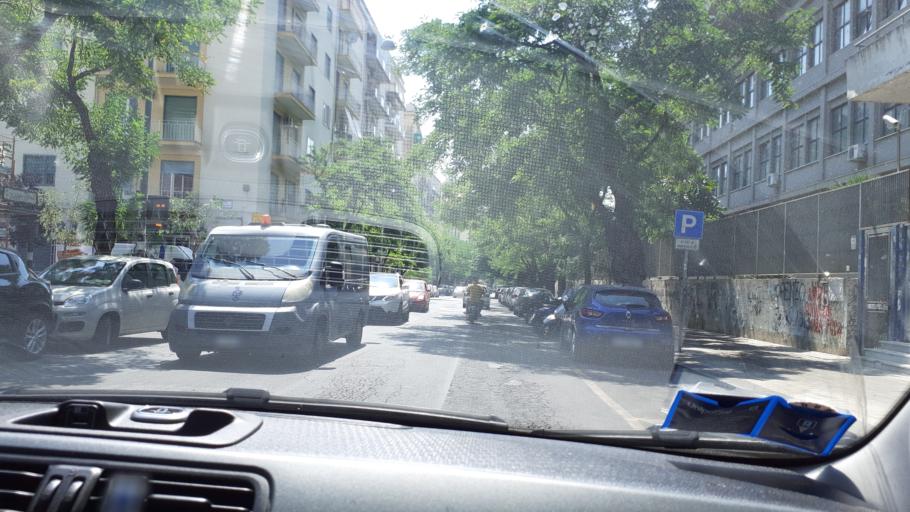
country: IT
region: Sicily
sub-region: Catania
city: Catania
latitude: 37.5104
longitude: 15.0751
